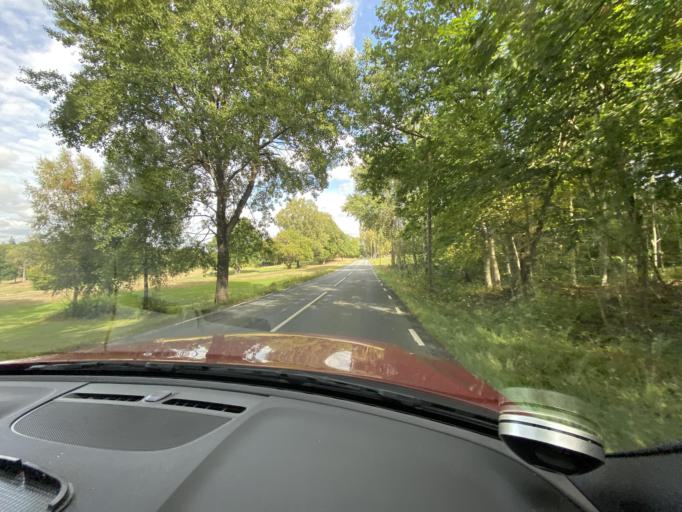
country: SE
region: Skane
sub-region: Hassleholms Kommun
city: Bjarnum
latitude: 56.3459
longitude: 13.7031
